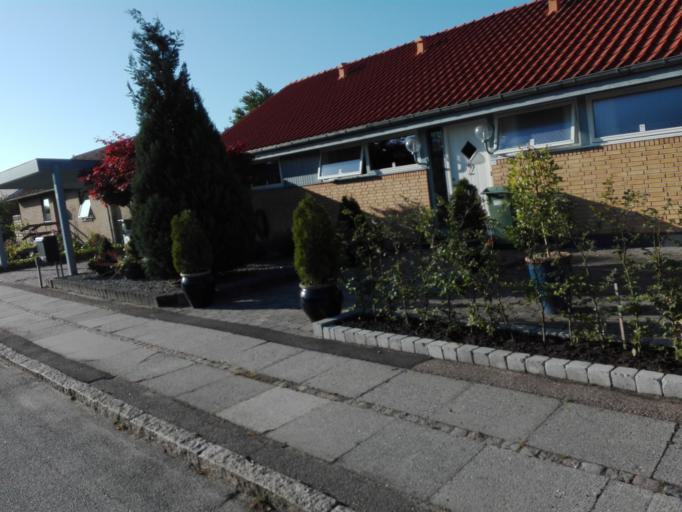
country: DK
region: Central Jutland
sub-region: Arhus Kommune
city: Tranbjerg
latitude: 56.0869
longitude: 10.1413
